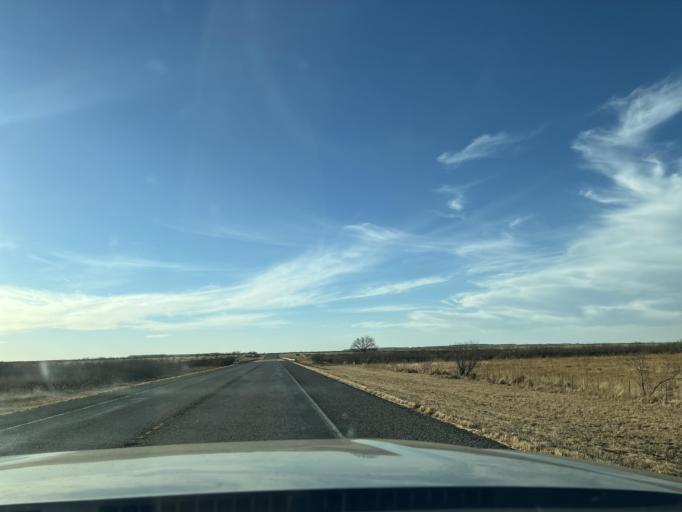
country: US
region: Texas
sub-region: Borden County
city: Gail
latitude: 32.7708
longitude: -101.3344
